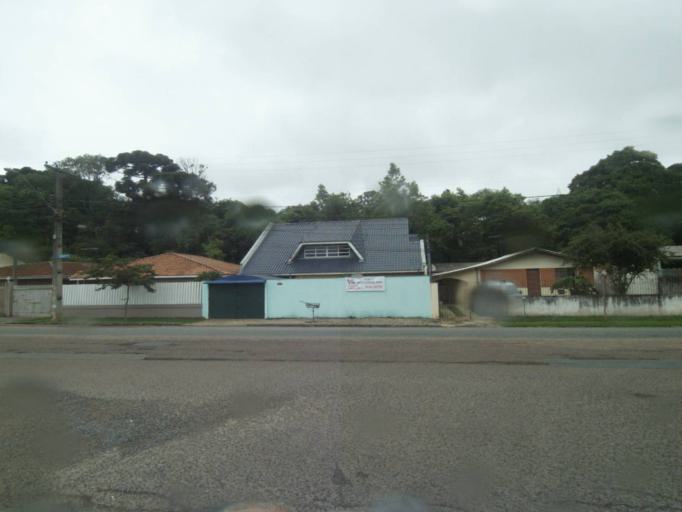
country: BR
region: Parana
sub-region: Curitiba
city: Curitiba
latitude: -25.4295
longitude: -49.3410
